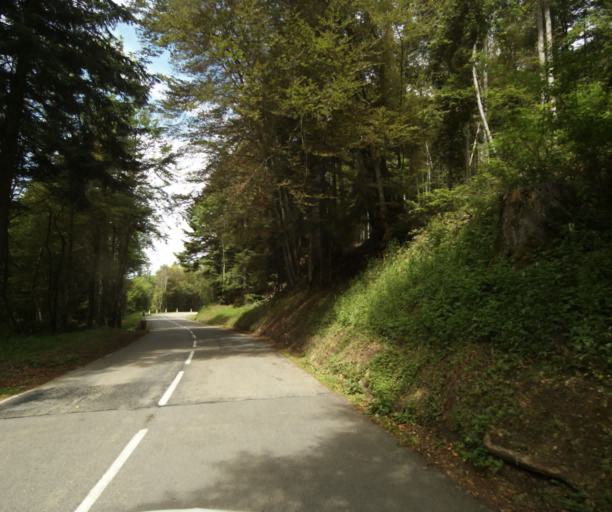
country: FR
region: Rhone-Alpes
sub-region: Departement de la Haute-Savoie
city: Perrignier
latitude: 46.2759
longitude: 6.4549
